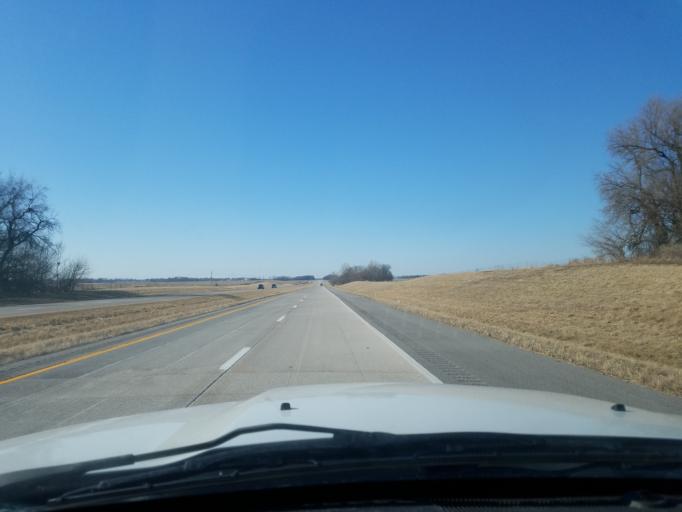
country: US
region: Kentucky
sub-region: Henderson County
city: Henderson
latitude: 37.7969
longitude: -87.5036
